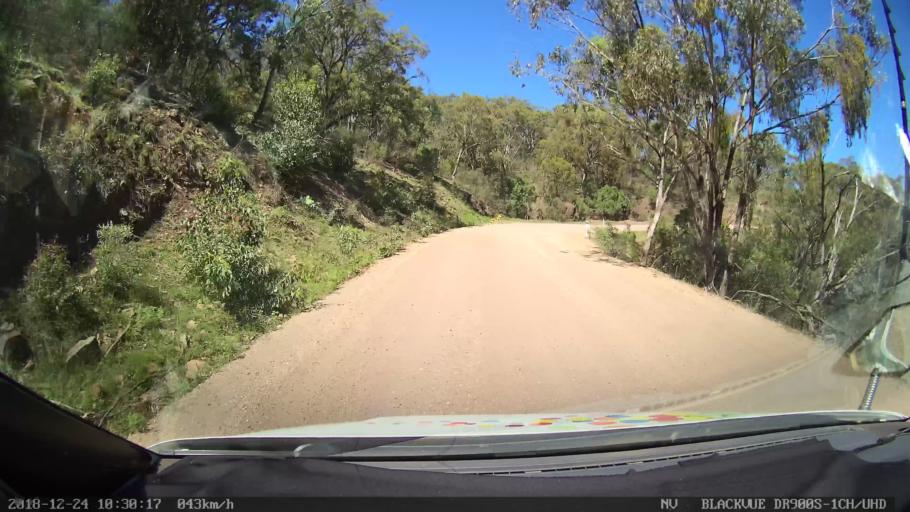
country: AU
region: New South Wales
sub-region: Upper Hunter Shire
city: Merriwa
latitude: -31.8361
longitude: 150.5260
